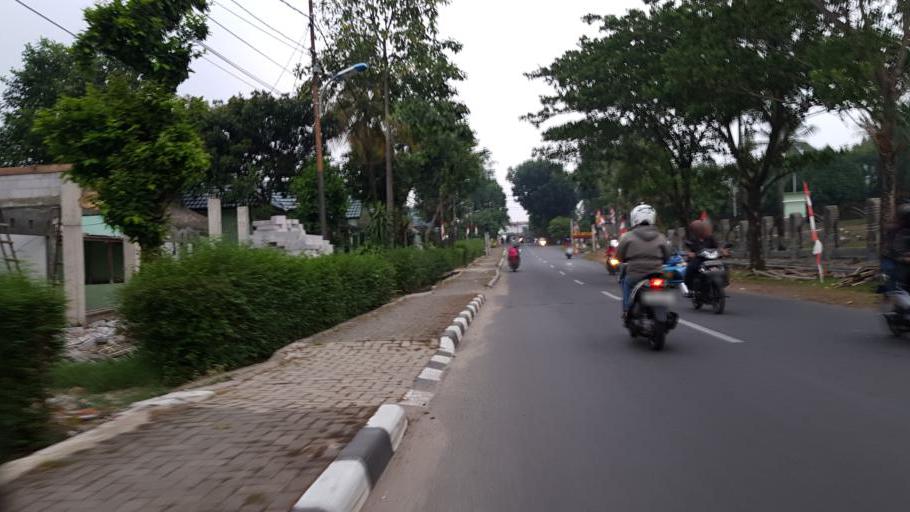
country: ID
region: West Java
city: Depok
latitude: -6.3292
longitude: 106.8453
